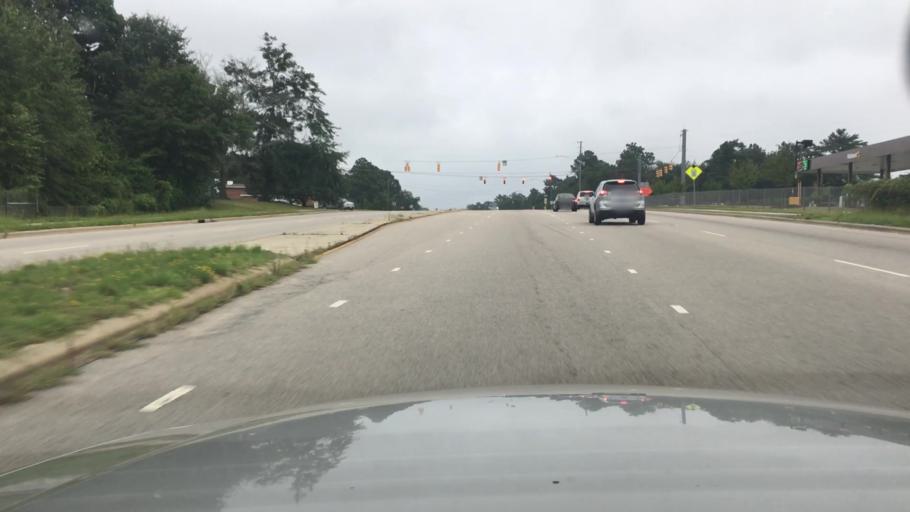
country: US
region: North Carolina
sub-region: Cumberland County
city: Hope Mills
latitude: 34.9845
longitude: -78.9321
